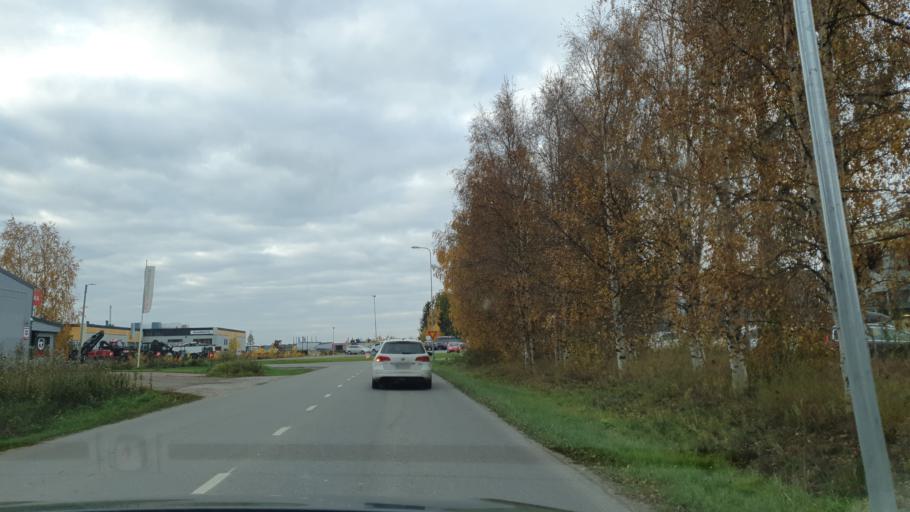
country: FI
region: Lapland
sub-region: Rovaniemi
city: Rovaniemi
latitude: 66.4939
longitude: 25.6659
